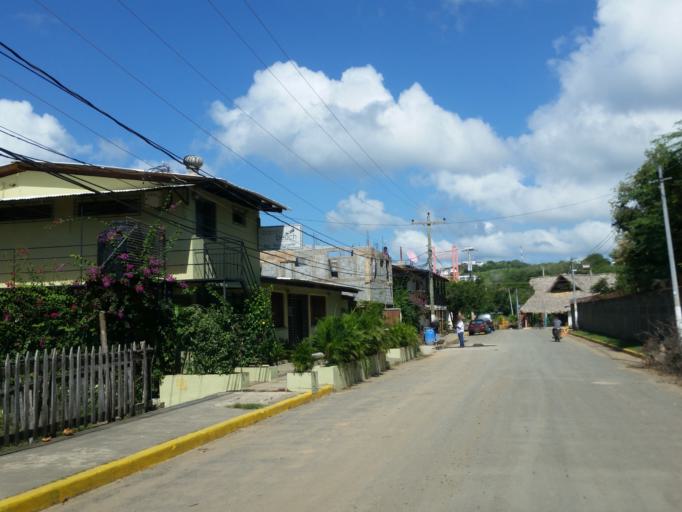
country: NI
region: Rivas
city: San Juan del Sur
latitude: 11.2580
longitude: -85.8733
